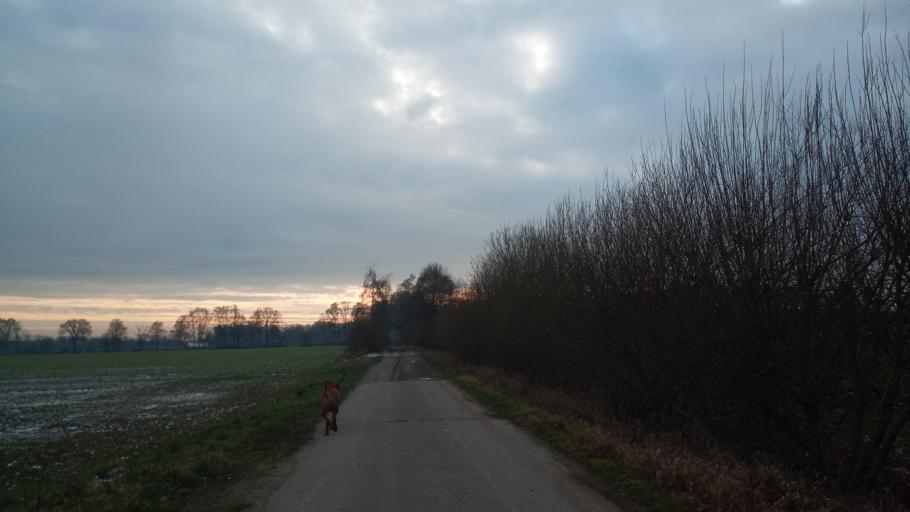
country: DE
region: Lower Saxony
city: Horstedt
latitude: 53.1629
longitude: 9.2500
